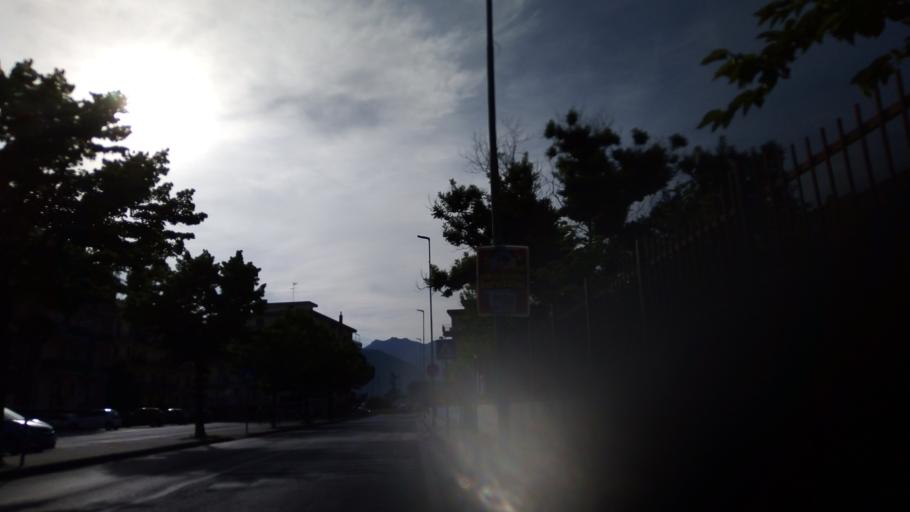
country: IT
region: Liguria
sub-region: Provincia di Savona
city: Borghetto Santo Spirito
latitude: 44.1130
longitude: 8.2408
